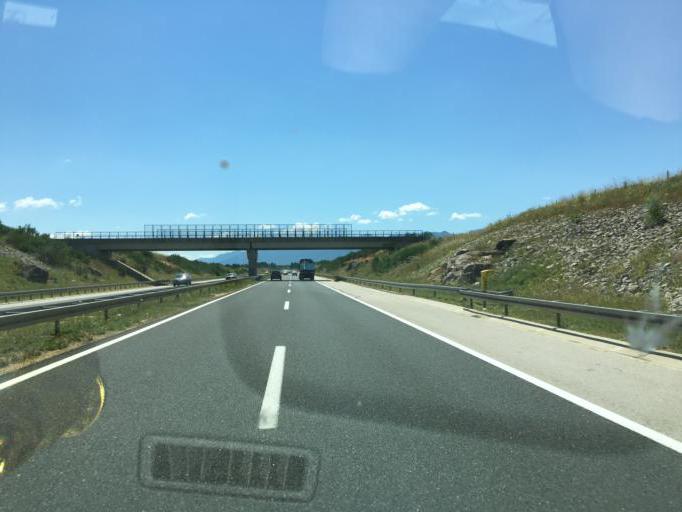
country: HR
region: Licko-Senjska
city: Gospic
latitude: 44.5554
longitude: 15.4304
